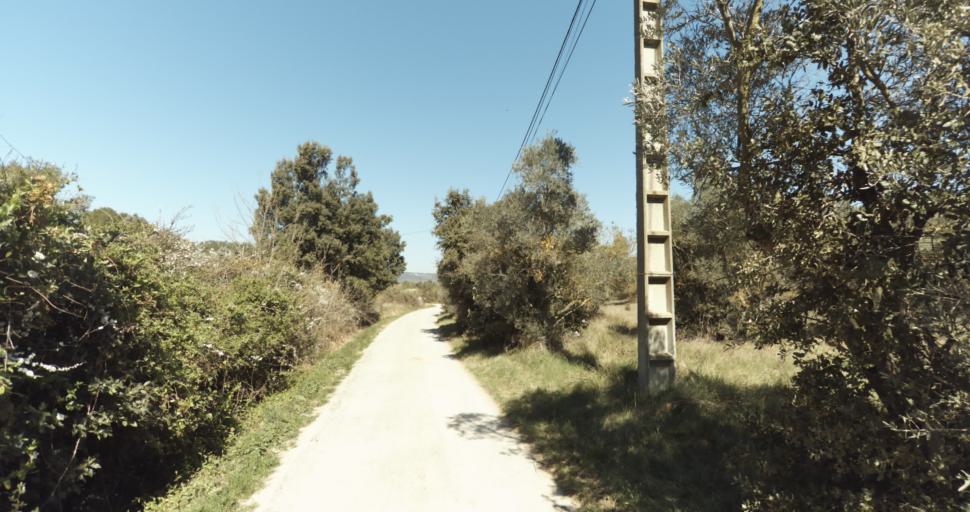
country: FR
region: Provence-Alpes-Cote d'Azur
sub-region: Departement des Bouches-du-Rhone
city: Pelissanne
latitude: 43.6146
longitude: 5.1577
